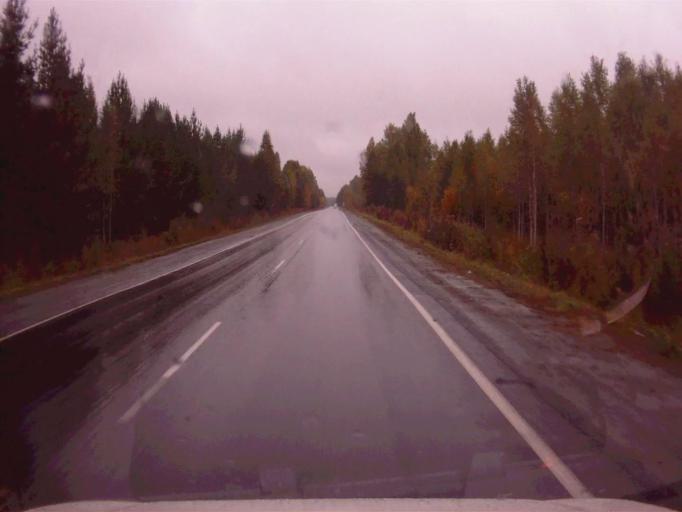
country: RU
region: Chelyabinsk
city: Tayginka
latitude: 55.5409
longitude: 60.6466
